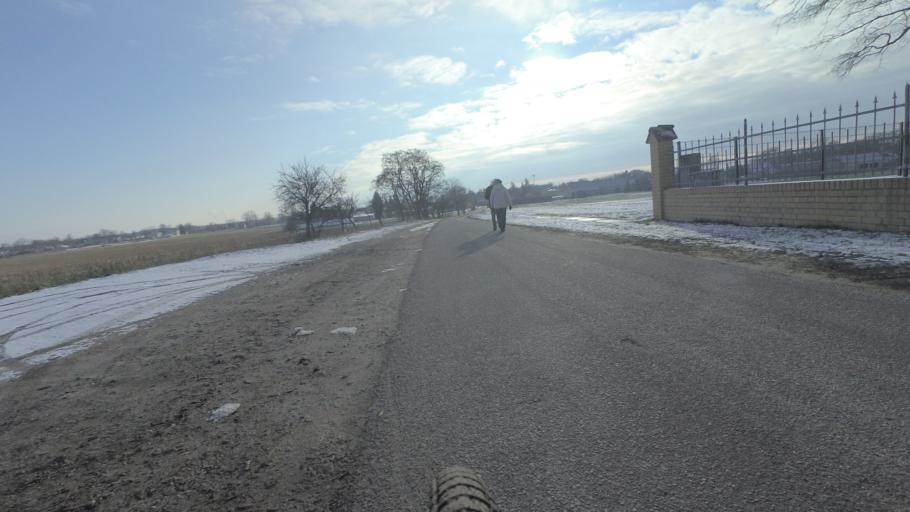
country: DE
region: Brandenburg
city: Zossen
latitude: 52.2290
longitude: 13.4169
